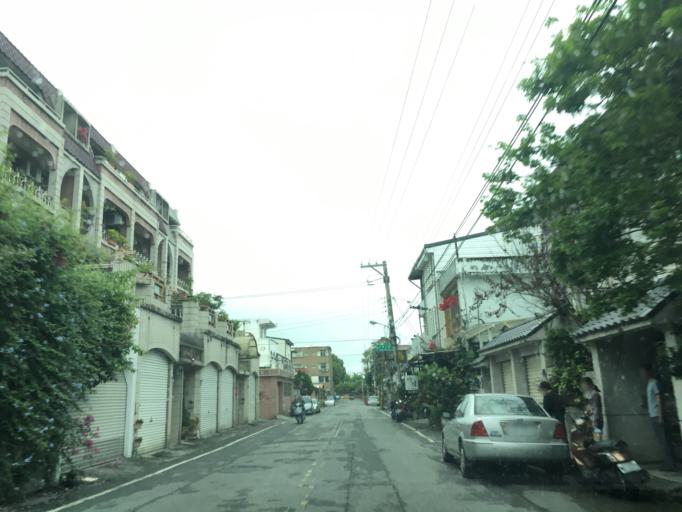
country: TW
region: Taiwan
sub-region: Hualien
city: Hualian
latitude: 23.9950
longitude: 121.5736
